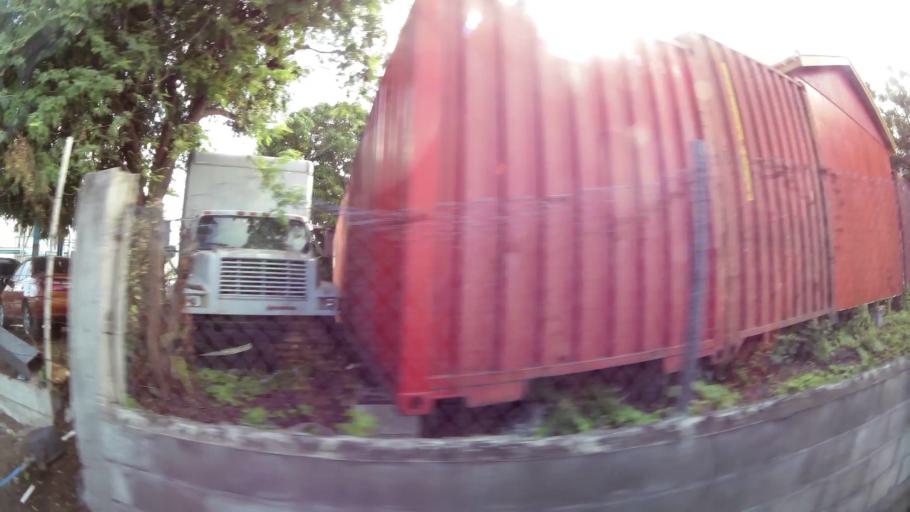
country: KN
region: Saint Paul Charlestown
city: Charlestown
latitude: 17.1337
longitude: -62.6268
